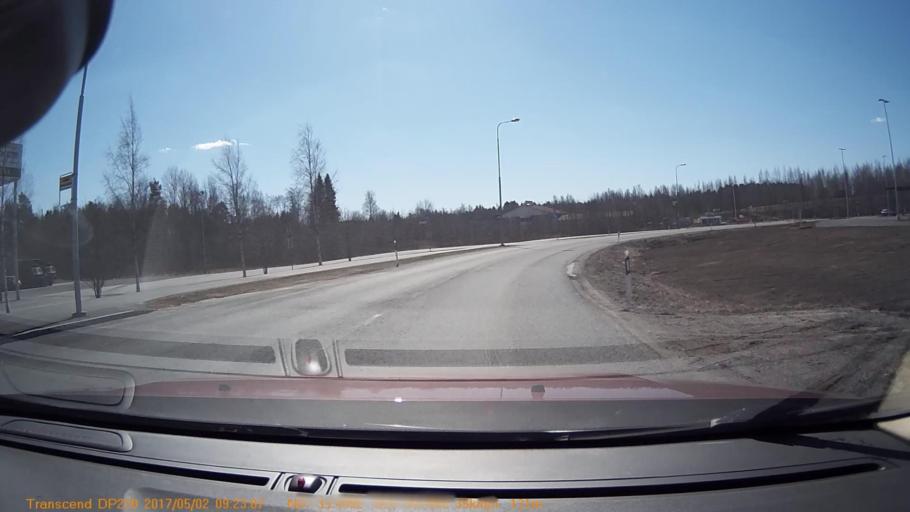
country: FI
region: Pirkanmaa
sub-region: Tampere
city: Yloejaervi
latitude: 61.5574
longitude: 23.5777
